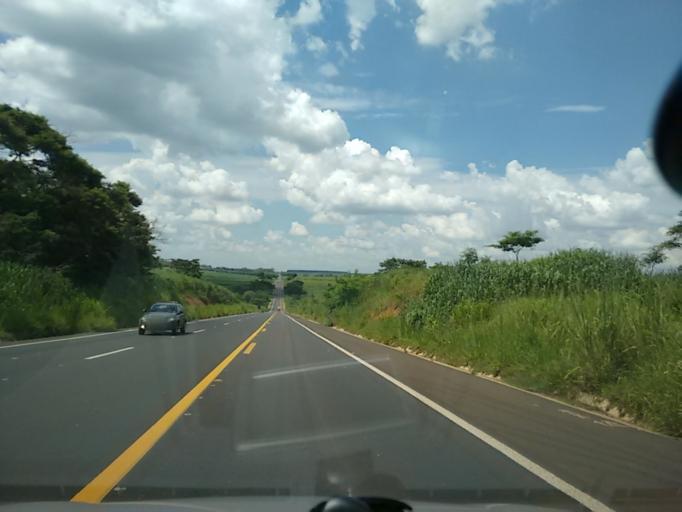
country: BR
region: Sao Paulo
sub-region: Osvaldo Cruz
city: Osvaldo Cruz
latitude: -21.8933
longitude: -50.8755
